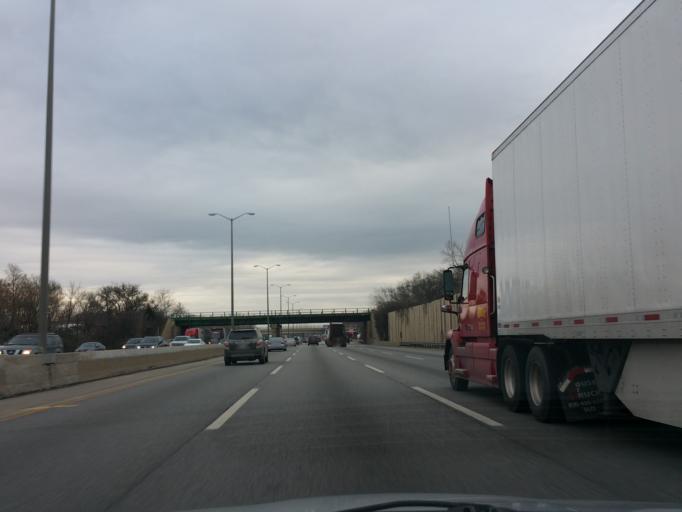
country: US
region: Illinois
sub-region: Cook County
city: Western Springs
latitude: 41.8081
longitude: -87.9127
